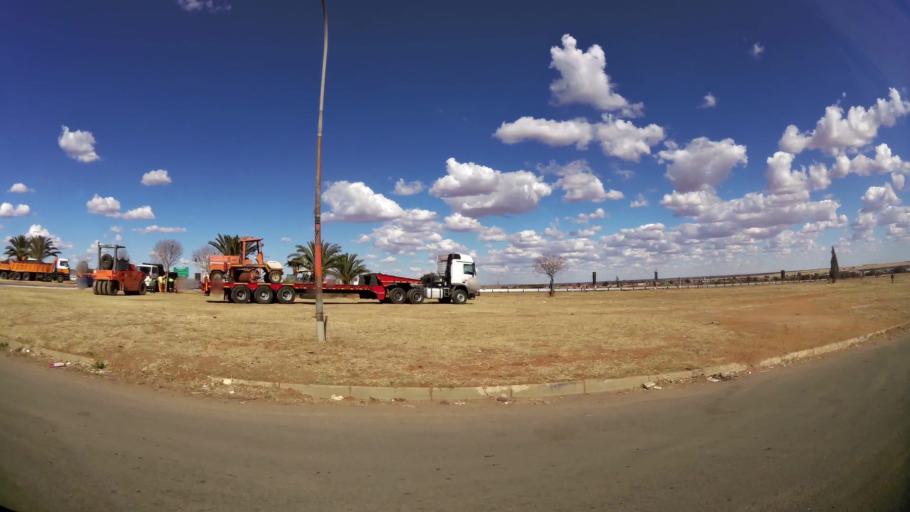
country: ZA
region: North-West
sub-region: Dr Kenneth Kaunda District Municipality
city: Klerksdorp
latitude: -26.8753
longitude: 26.5897
